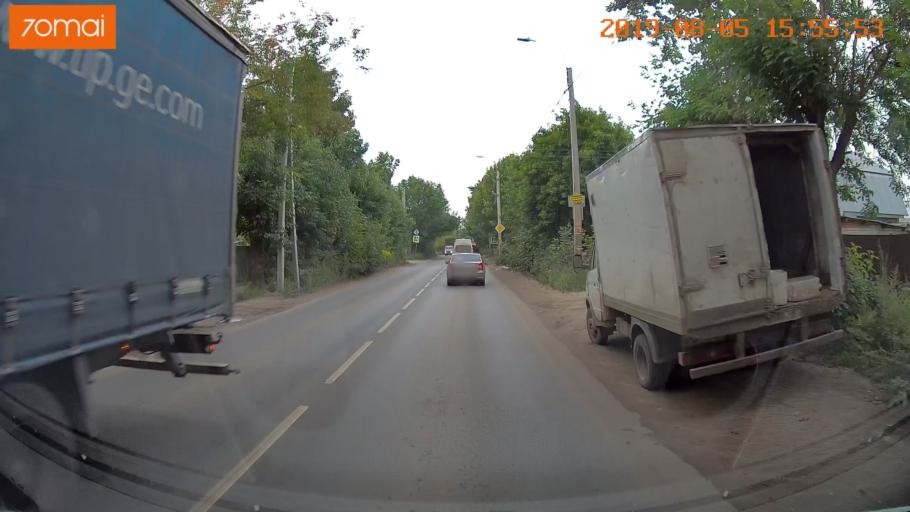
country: RU
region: Ivanovo
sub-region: Gorod Ivanovo
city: Ivanovo
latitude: 56.9953
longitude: 40.9516
